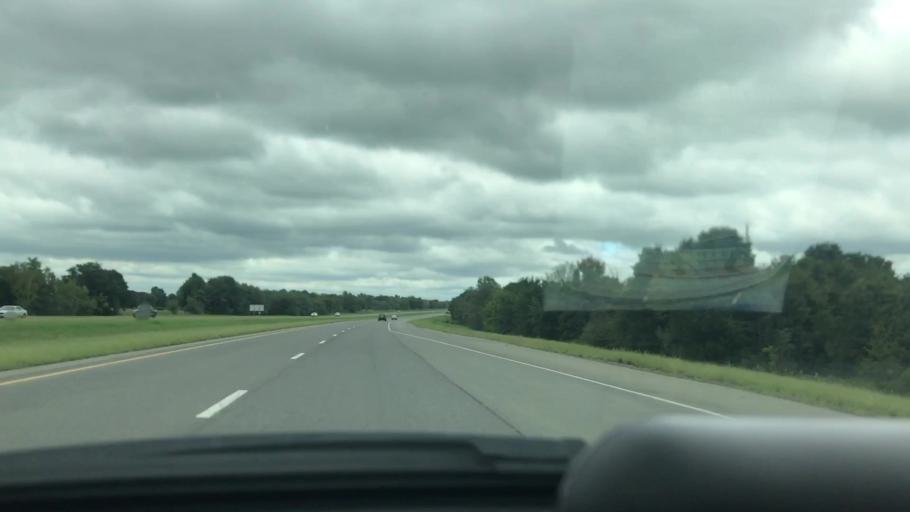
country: US
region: Oklahoma
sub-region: McIntosh County
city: Checotah
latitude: 35.5802
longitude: -95.4907
